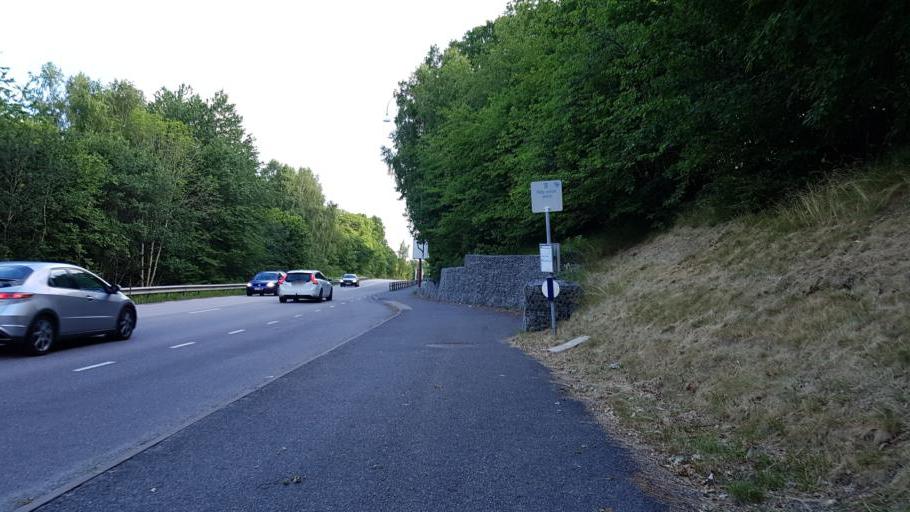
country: SE
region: Vaestra Goetaland
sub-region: Harryda Kommun
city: Molnlycke
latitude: 57.6664
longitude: 12.0921
